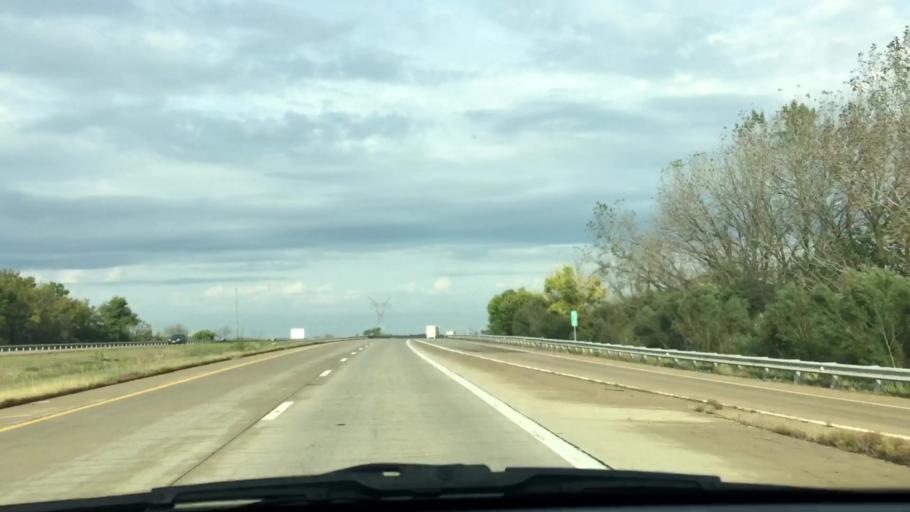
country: US
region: Illinois
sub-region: Whiteside County
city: Sterling
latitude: 41.7609
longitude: -89.7870
